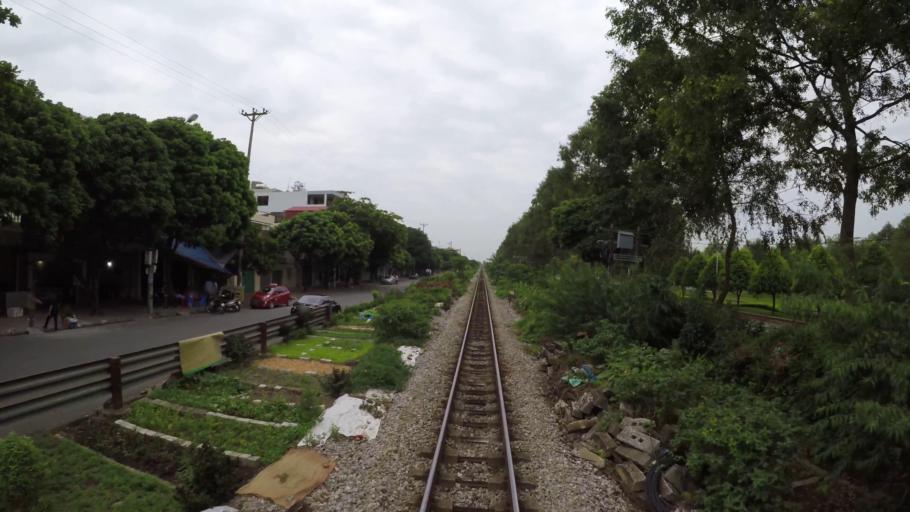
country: VN
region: Hai Duong
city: Thanh Pho Hai Duong
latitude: 20.9440
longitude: 106.3527
